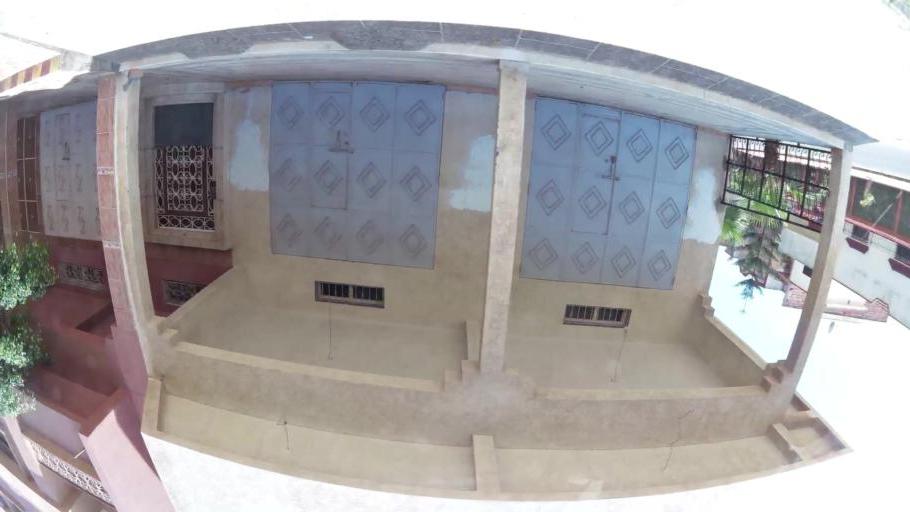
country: MA
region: Gharb-Chrarda-Beni Hssen
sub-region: Kenitra Province
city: Kenitra
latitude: 34.2664
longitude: -6.6198
